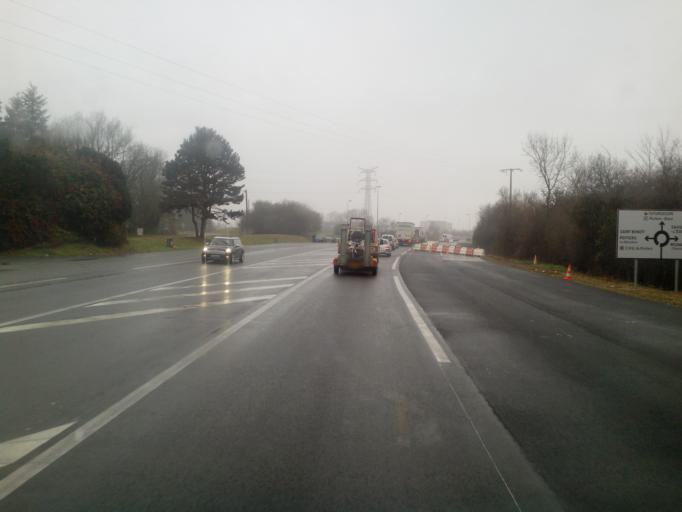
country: FR
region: Poitou-Charentes
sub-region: Departement de la Vienne
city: Mignaloux-Beauvoir
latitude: 46.5516
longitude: 0.4010
